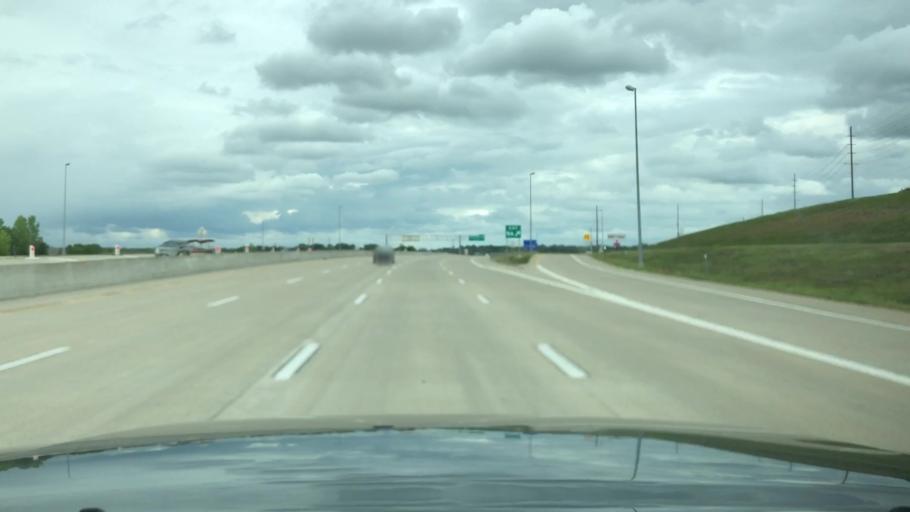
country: US
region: Missouri
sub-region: Saint Charles County
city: Cottleville
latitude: 38.7397
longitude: -90.6230
